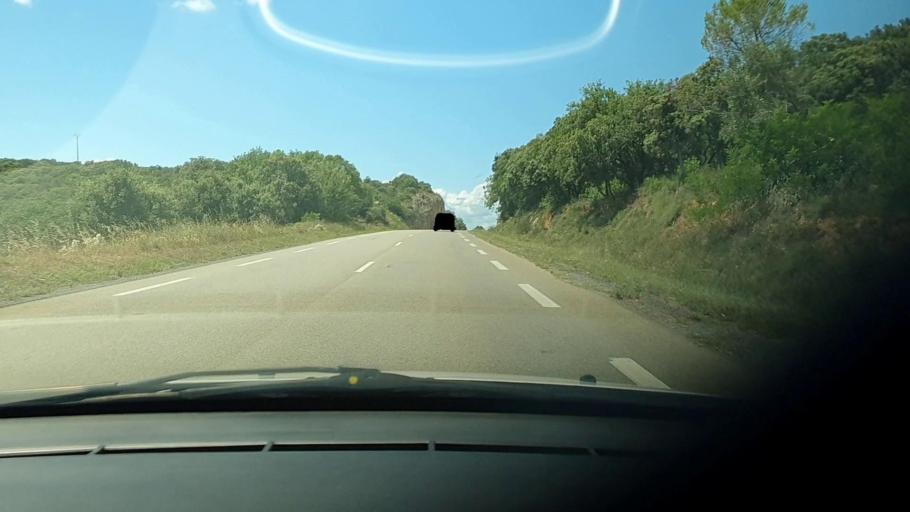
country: FR
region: Languedoc-Roussillon
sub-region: Departement du Gard
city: Moussac
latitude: 44.0623
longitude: 4.2588
